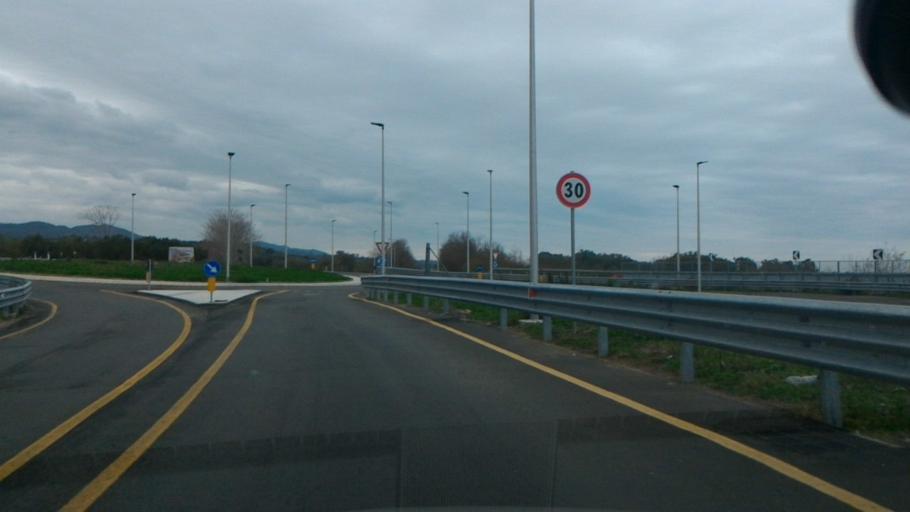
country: IT
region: Calabria
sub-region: Provincia di Crotone
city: Ciro
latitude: 39.4198
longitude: 17.0789
